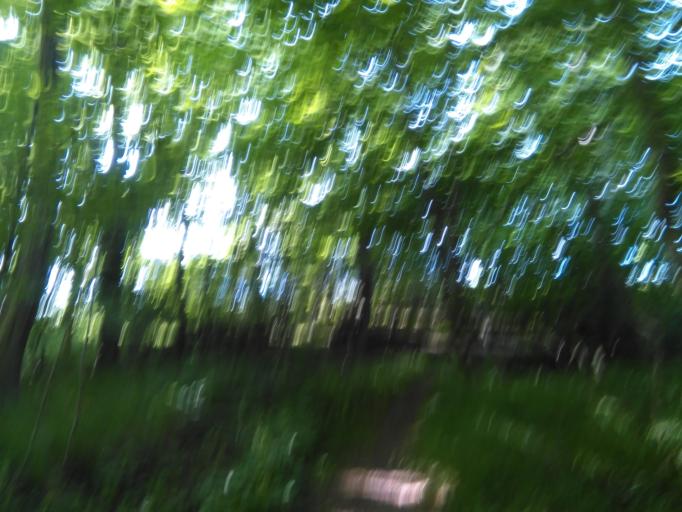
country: DK
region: Capital Region
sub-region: Bornholm Kommune
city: Akirkeby
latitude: 55.2255
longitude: 14.8793
